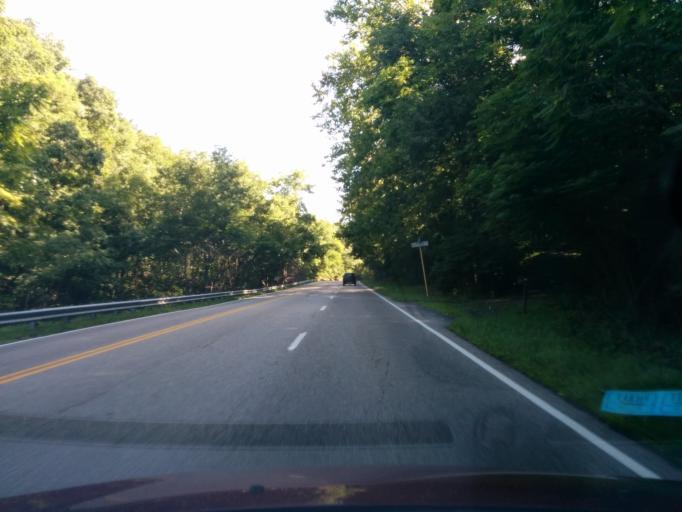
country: US
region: Virginia
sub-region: City of Lexington
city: Lexington
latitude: 37.7218
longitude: -79.4701
